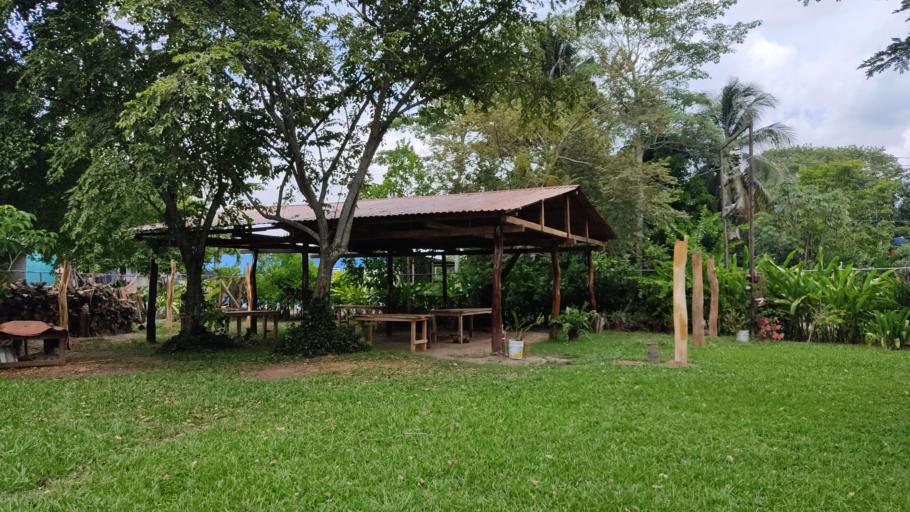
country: MX
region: Tabasco
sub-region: Comalcalco
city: Betania
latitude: 18.2830
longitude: -93.3098
